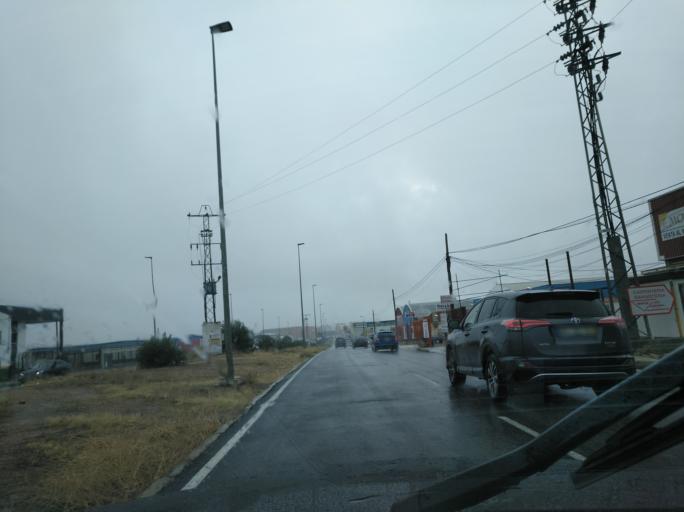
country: ES
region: Extremadura
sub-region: Provincia de Badajoz
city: Badajoz
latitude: 38.8953
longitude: -6.9919
